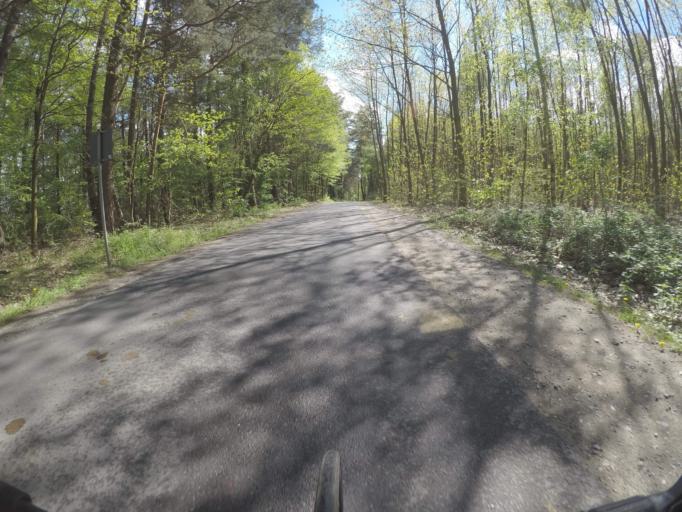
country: DE
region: Brandenburg
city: Bernau bei Berlin
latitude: 52.7119
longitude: 13.5911
